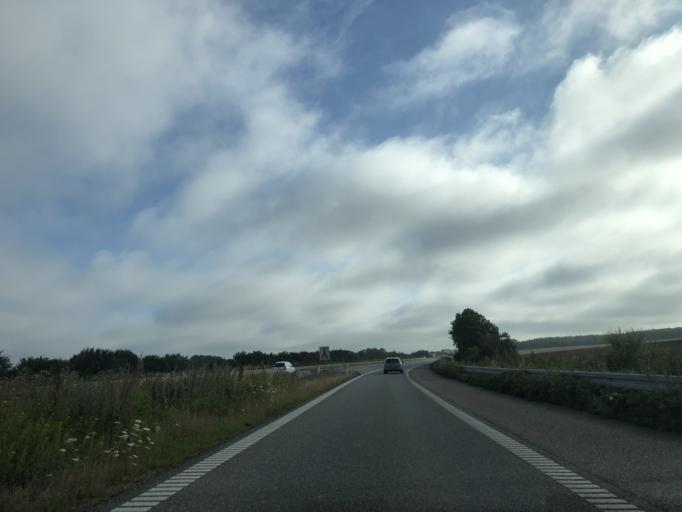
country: DK
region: Central Jutland
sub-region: Arhus Kommune
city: Kolt
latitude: 56.1096
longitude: 10.0558
